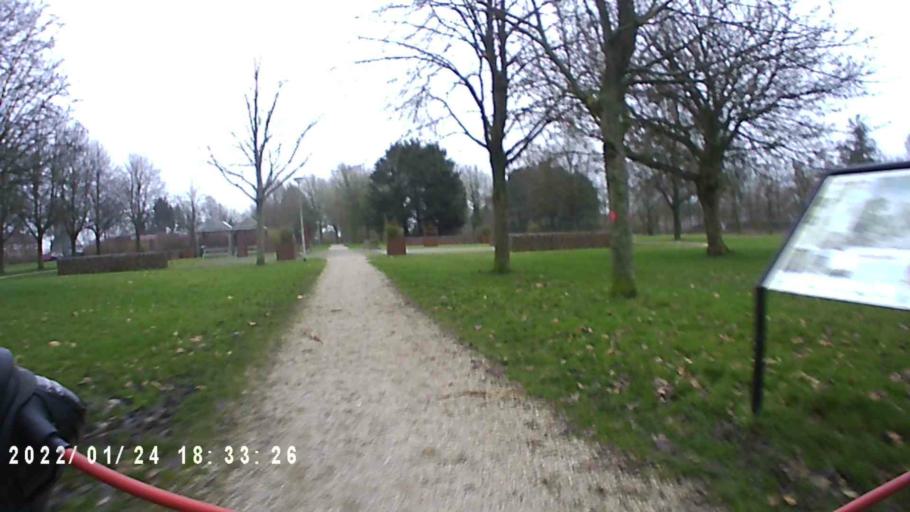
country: NL
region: Groningen
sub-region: Gemeente De Marne
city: Ulrum
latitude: 53.3570
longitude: 6.3348
